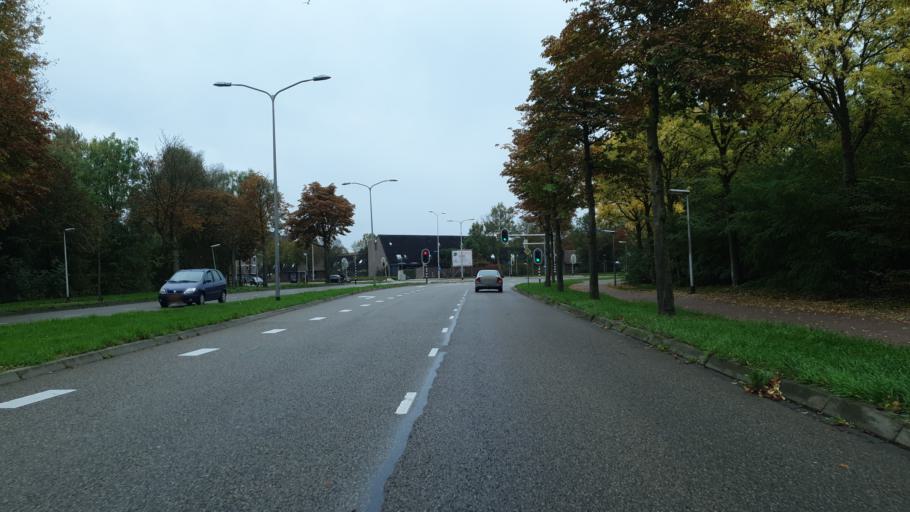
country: NL
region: Gelderland
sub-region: Gemeente Nijmegen
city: Lindenholt
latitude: 51.8307
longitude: 5.7961
